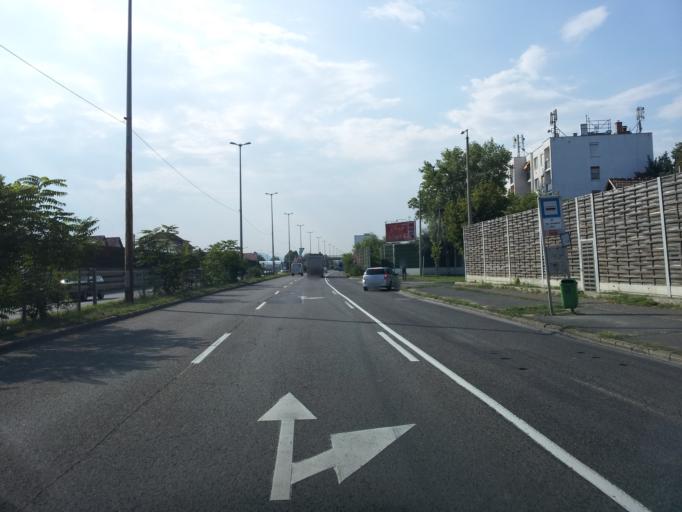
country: HU
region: Budapest
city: Budapest XIX. keruelet
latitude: 47.4393
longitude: 19.1381
